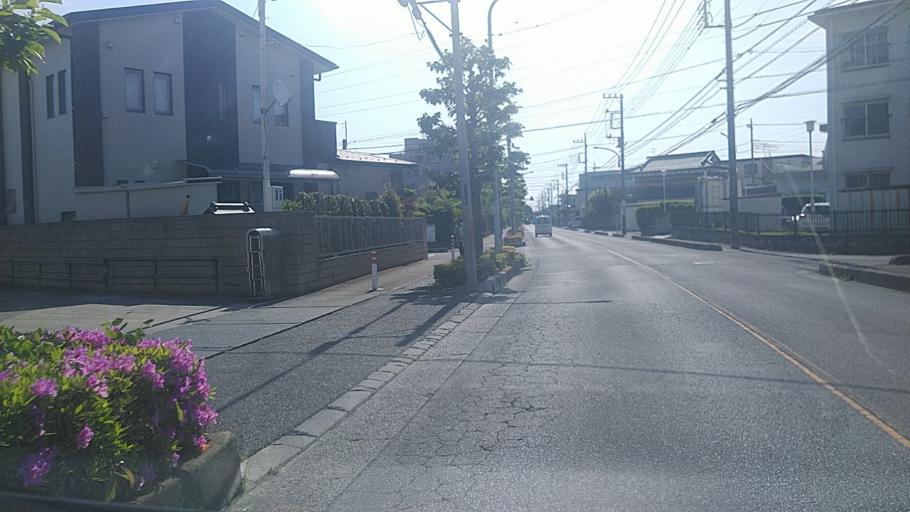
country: JP
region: Saitama
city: Koshigaya
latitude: 35.8785
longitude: 139.7511
